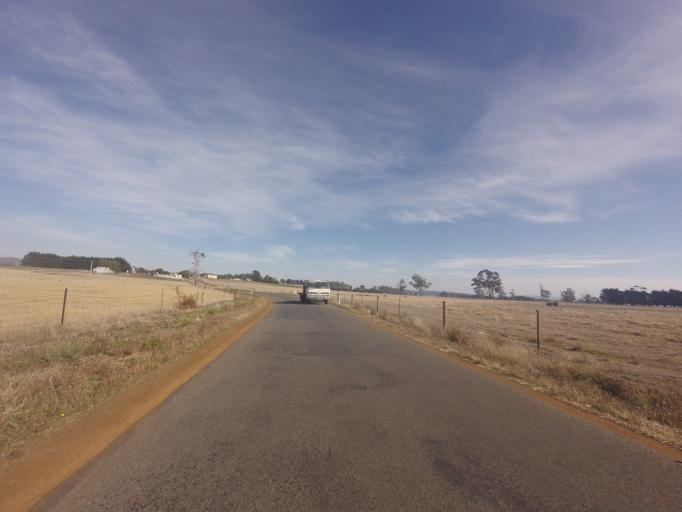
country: AU
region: Tasmania
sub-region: Sorell
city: Sorell
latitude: -42.4484
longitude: 147.4625
